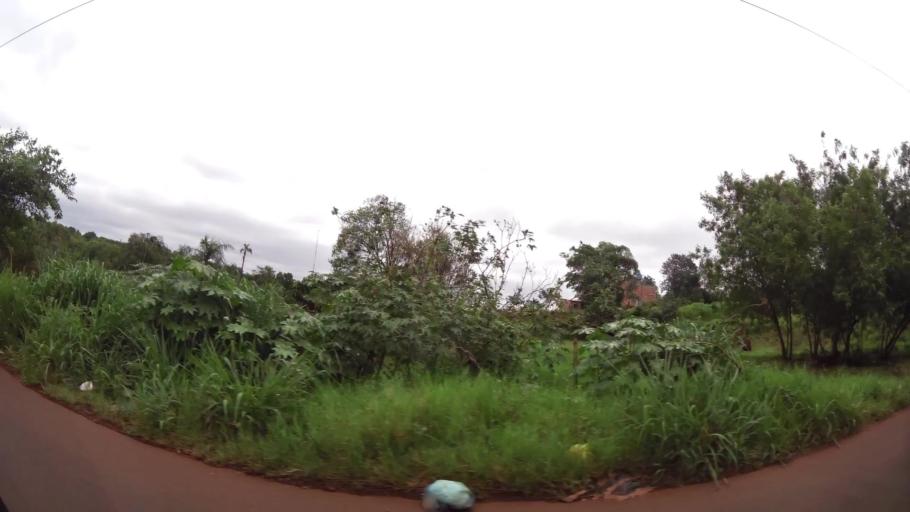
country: PY
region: Alto Parana
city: Ciudad del Este
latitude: -25.4992
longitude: -54.6877
